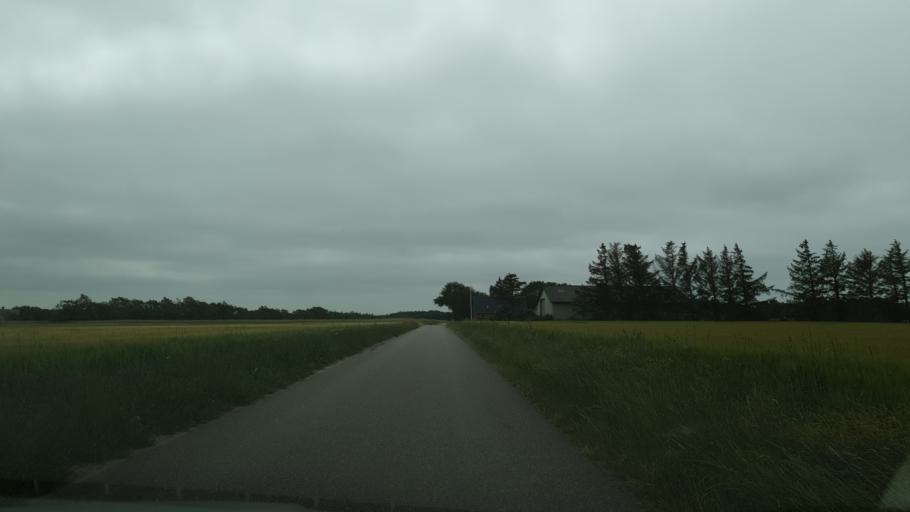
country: DK
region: Central Jutland
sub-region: Ringkobing-Skjern Kommune
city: Skjern
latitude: 55.9477
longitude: 8.4040
